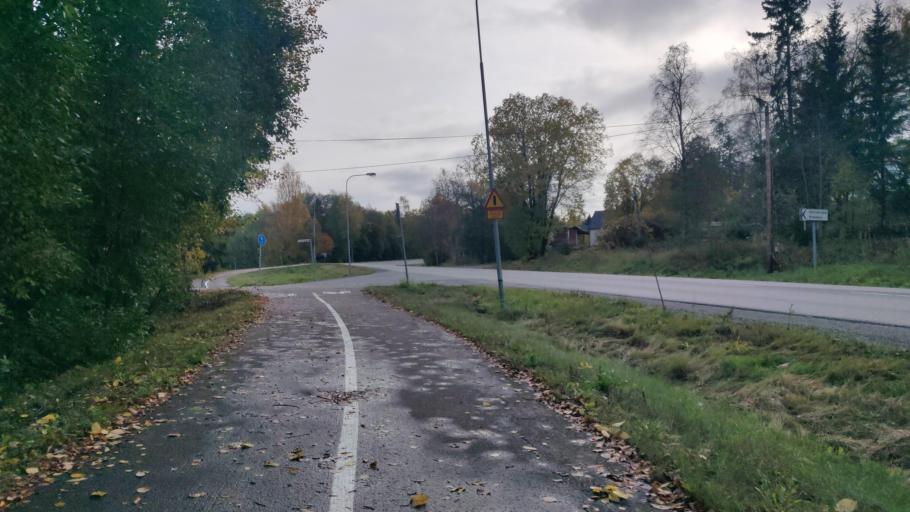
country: SE
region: Vaesternorrland
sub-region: Sundsvalls Kommun
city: Sundsbruk
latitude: 62.4366
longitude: 17.3412
